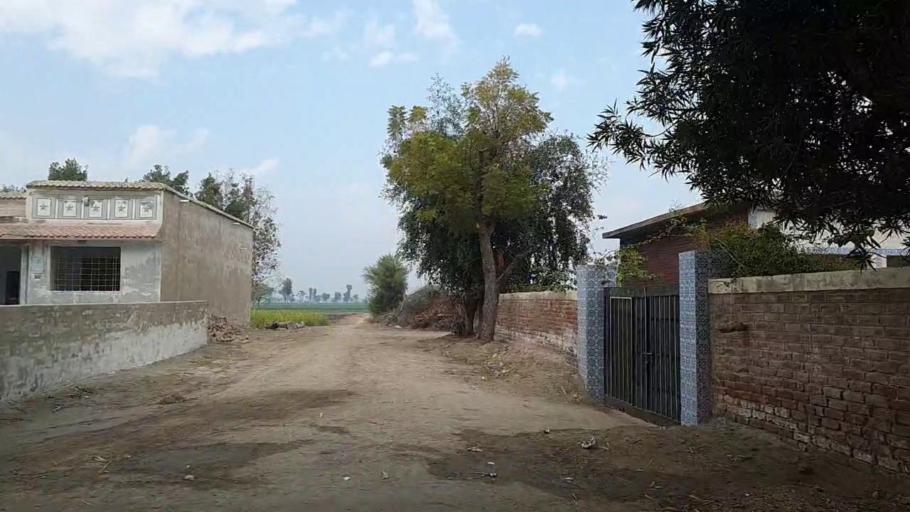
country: PK
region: Sindh
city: Daur
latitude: 26.3633
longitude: 68.3794
